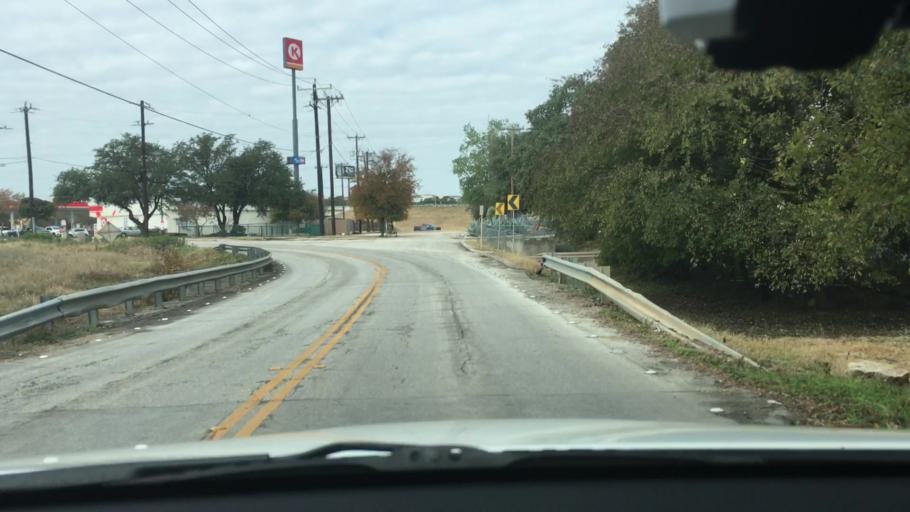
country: US
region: Texas
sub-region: Bexar County
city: Hollywood Park
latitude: 29.5992
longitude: -98.4160
